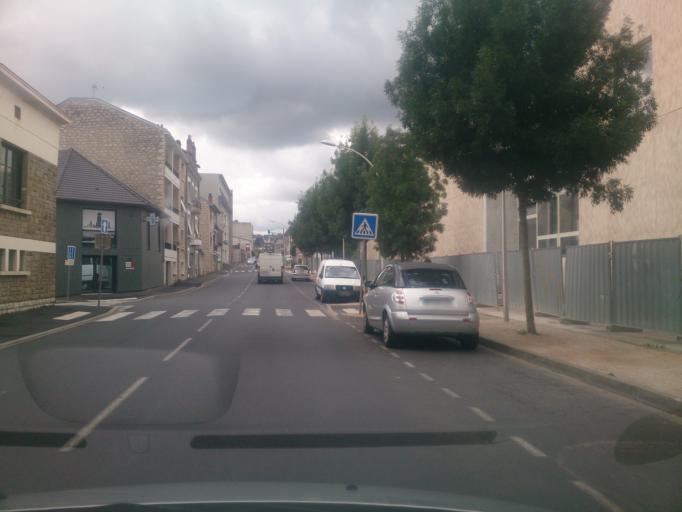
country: FR
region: Limousin
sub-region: Departement de la Correze
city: Brive-la-Gaillarde
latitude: 45.1603
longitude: 1.5407
